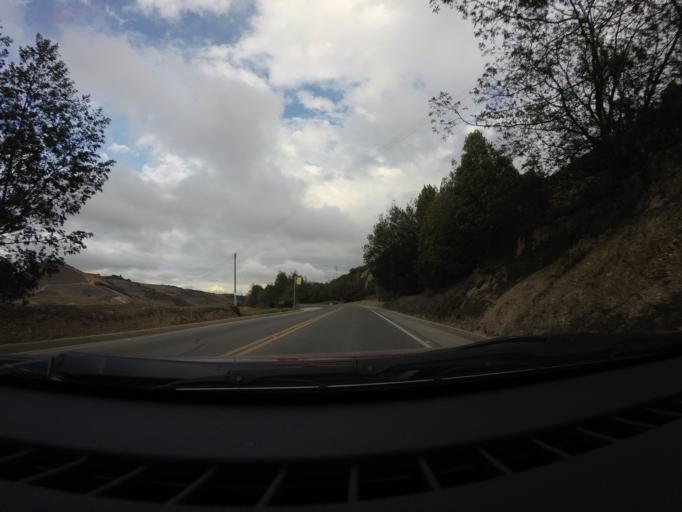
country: CO
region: Boyaca
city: Cucaita
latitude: 5.5647
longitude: -73.4157
